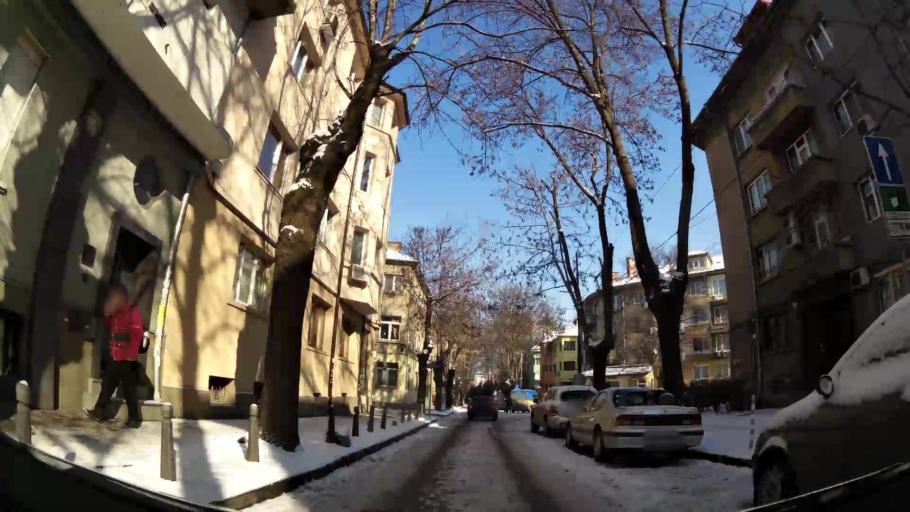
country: BG
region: Sofia-Capital
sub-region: Stolichna Obshtina
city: Sofia
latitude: 42.6842
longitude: 23.3288
